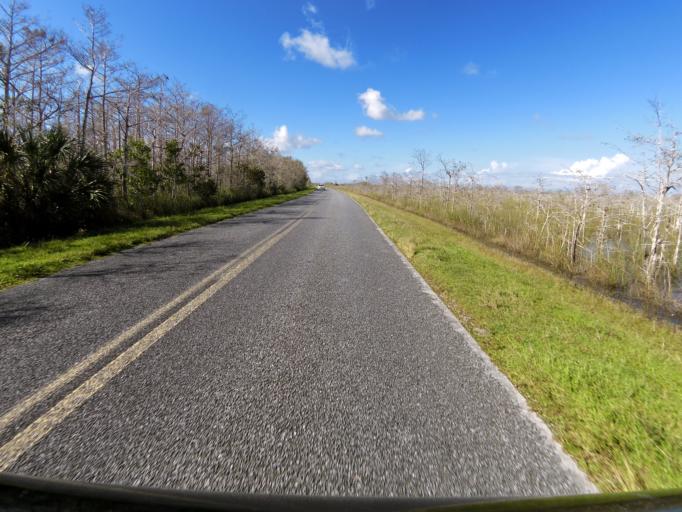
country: US
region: Florida
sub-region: Miami-Dade County
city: Florida City
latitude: 25.4313
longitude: -80.7750
